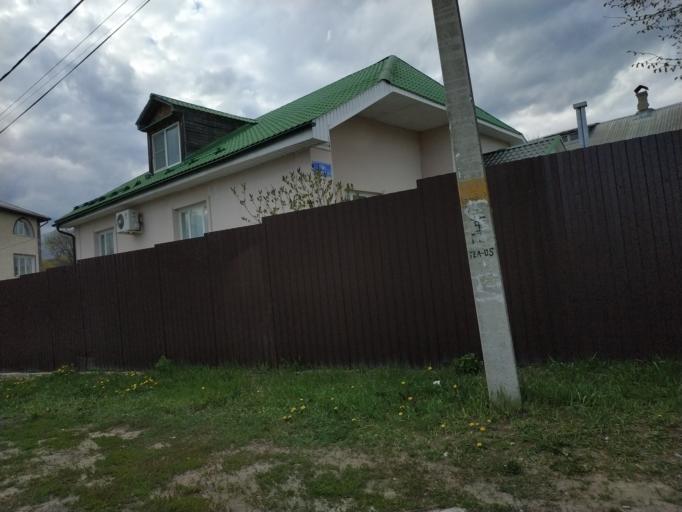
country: RU
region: Moskovskaya
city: Pavlovskiy Posad
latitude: 55.7799
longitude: 38.6475
